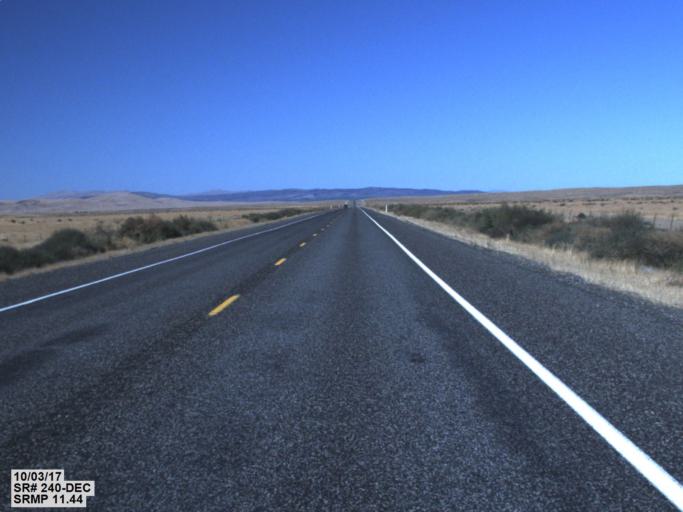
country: US
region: Washington
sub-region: Benton County
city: Benton City
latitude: 46.4739
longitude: -119.5561
